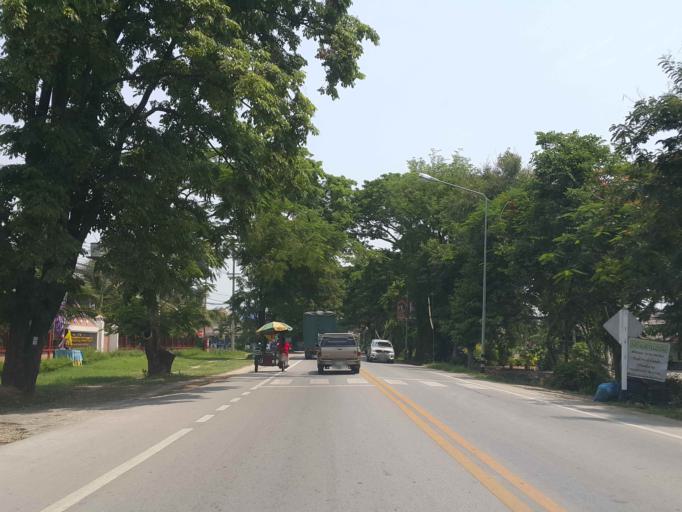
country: TH
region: Chiang Mai
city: Mae Taeng
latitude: 19.0370
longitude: 98.9689
